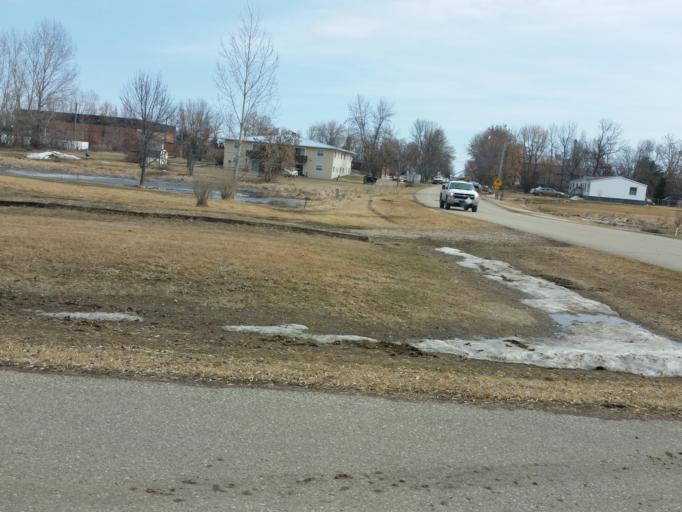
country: US
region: North Dakota
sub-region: Walsh County
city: Grafton
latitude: 48.2936
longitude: -97.3782
